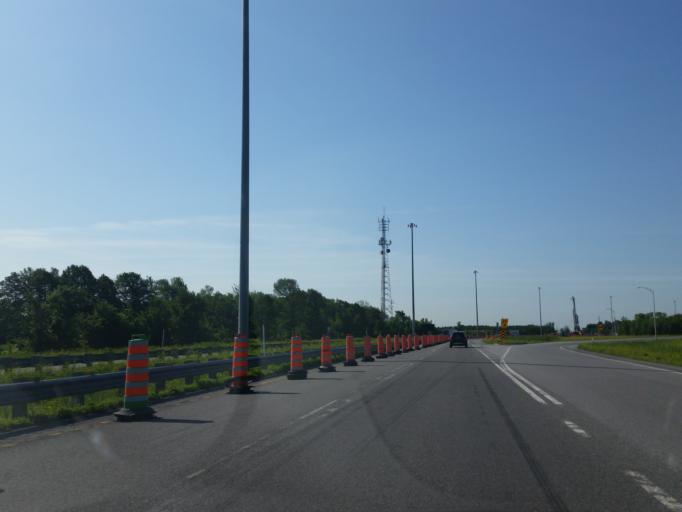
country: CA
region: Quebec
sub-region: Monteregie
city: Napierville
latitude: 45.2709
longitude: -73.4699
